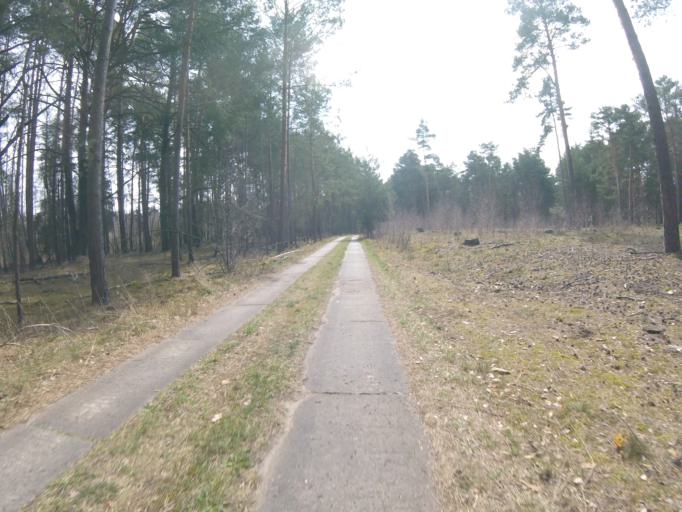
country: DE
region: Brandenburg
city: Schwerin
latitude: 52.1801
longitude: 13.6346
